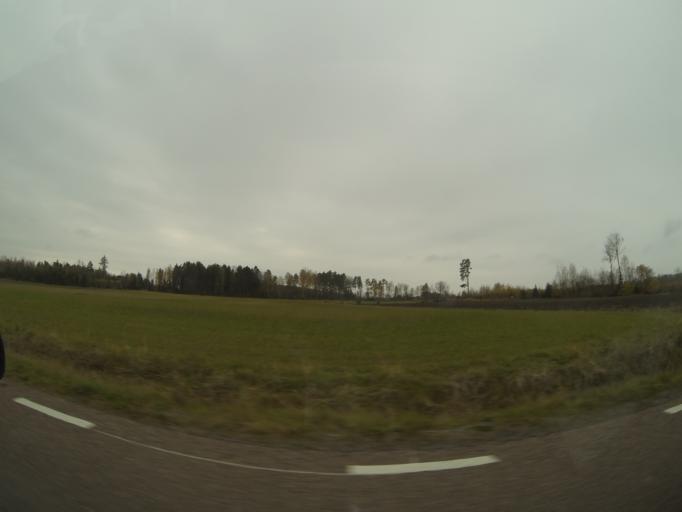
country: SE
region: Vaestmanland
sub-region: Hallstahammars Kommun
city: Hallstahammar
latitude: 59.5452
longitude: 16.1245
